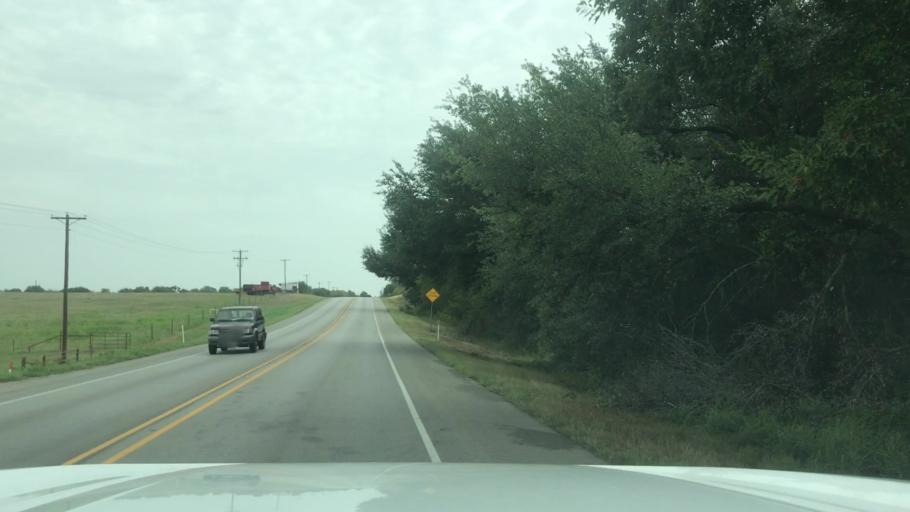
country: US
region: Texas
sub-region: Erath County
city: Dublin
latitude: 32.0930
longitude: -98.4155
